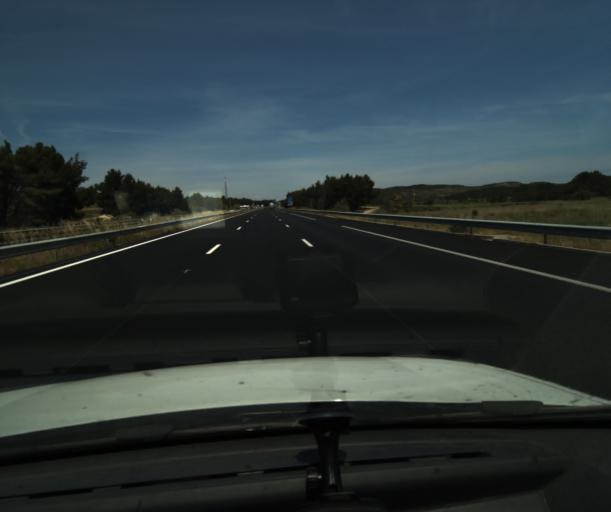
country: FR
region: Languedoc-Roussillon
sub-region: Departement de l'Aude
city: Peyriac-de-Mer
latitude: 43.1084
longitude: 2.9498
